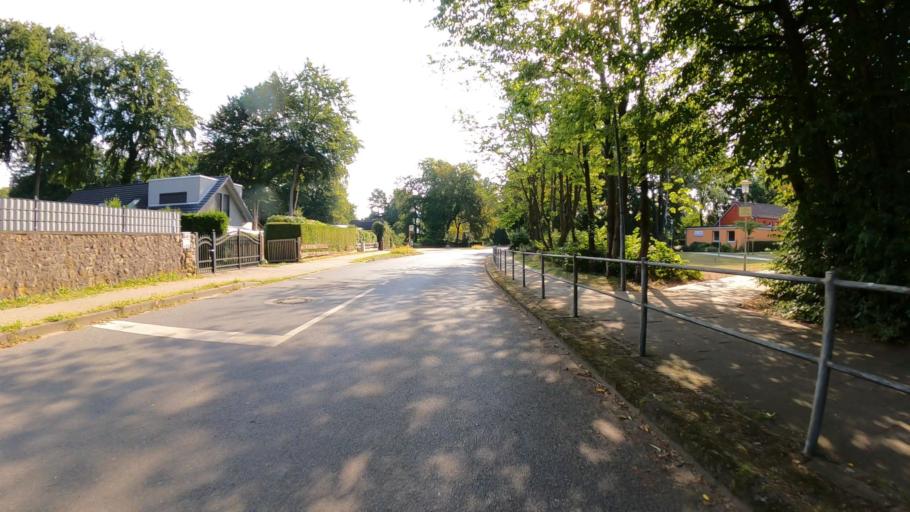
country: DE
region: Schleswig-Holstein
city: Hohenhorn
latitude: 53.4938
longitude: 10.3546
